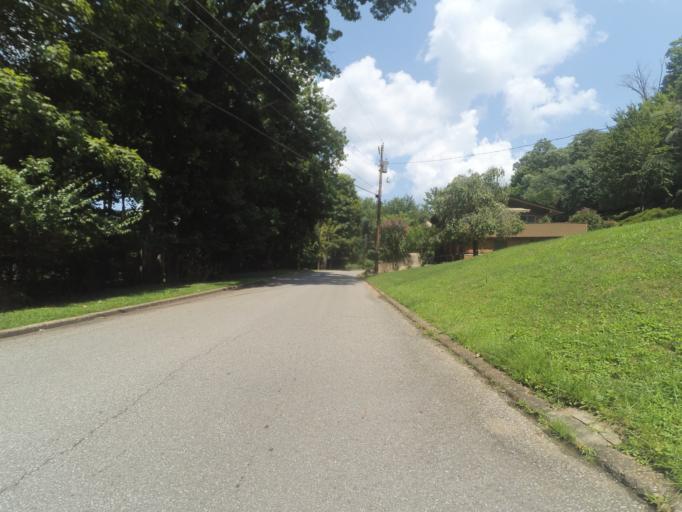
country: US
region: West Virginia
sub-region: Cabell County
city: Huntington
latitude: 38.3964
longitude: -82.4307
